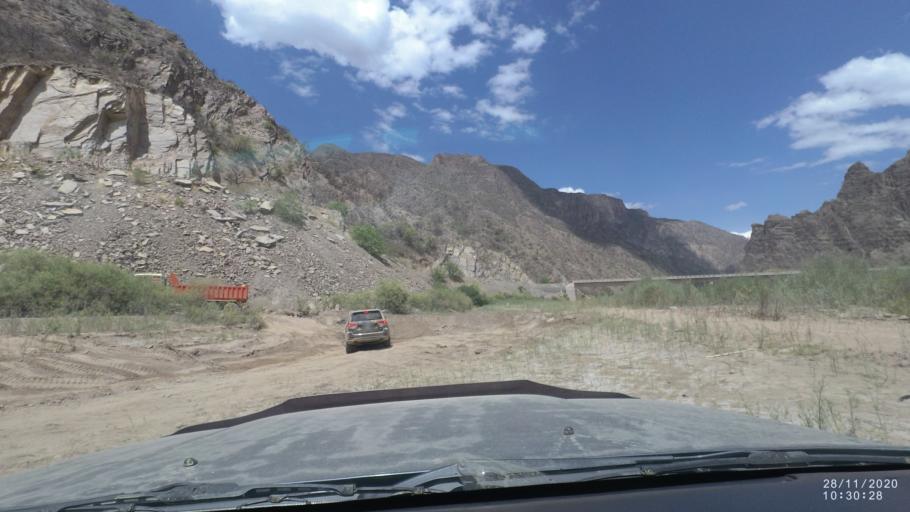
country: BO
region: Cochabamba
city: Capinota
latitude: -17.7954
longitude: -66.1356
